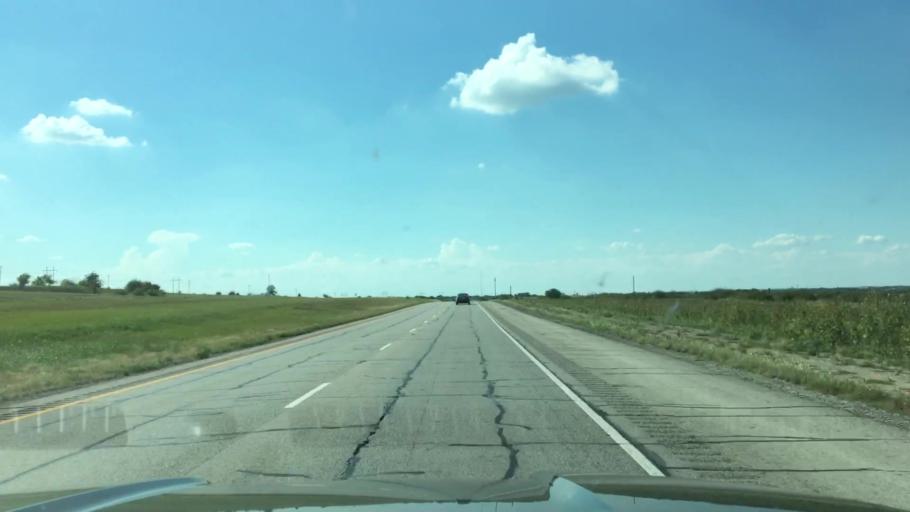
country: US
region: Texas
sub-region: Wise County
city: New Fairview
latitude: 33.1545
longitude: -97.5151
